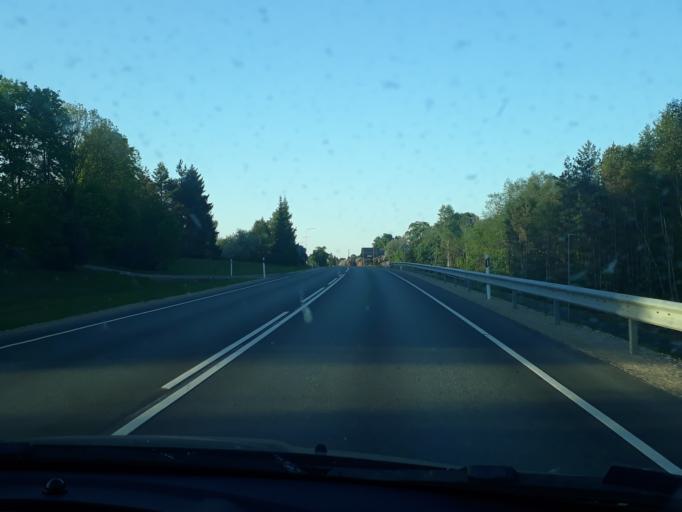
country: EE
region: Paernumaa
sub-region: Tootsi vald
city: Tootsi
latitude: 58.5141
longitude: 24.8149
